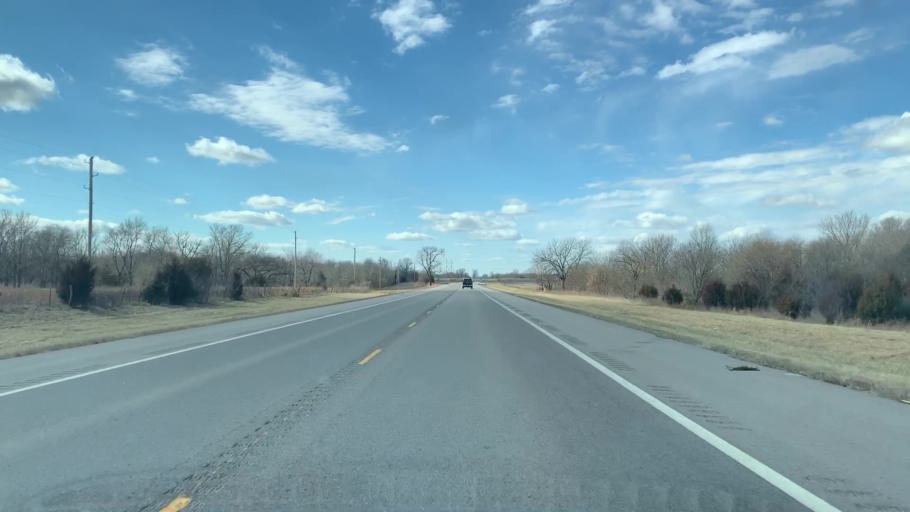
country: US
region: Kansas
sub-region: Labette County
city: Oswego
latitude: 37.3400
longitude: -95.0705
